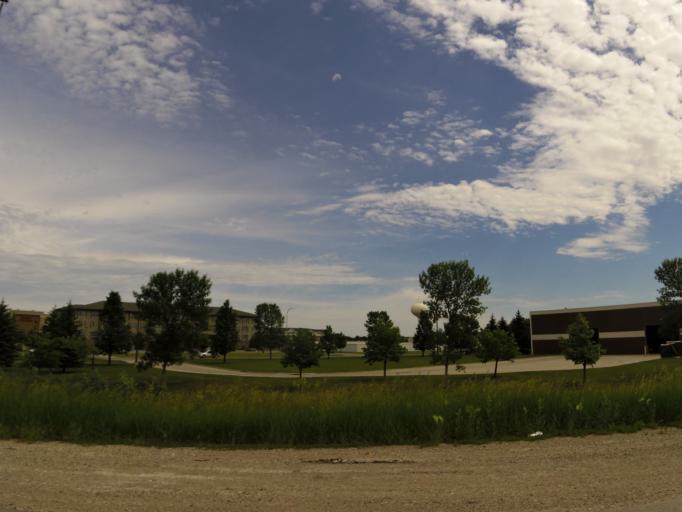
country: US
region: North Dakota
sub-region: Grand Forks County
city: Grand Forks
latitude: 47.8902
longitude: -97.0867
